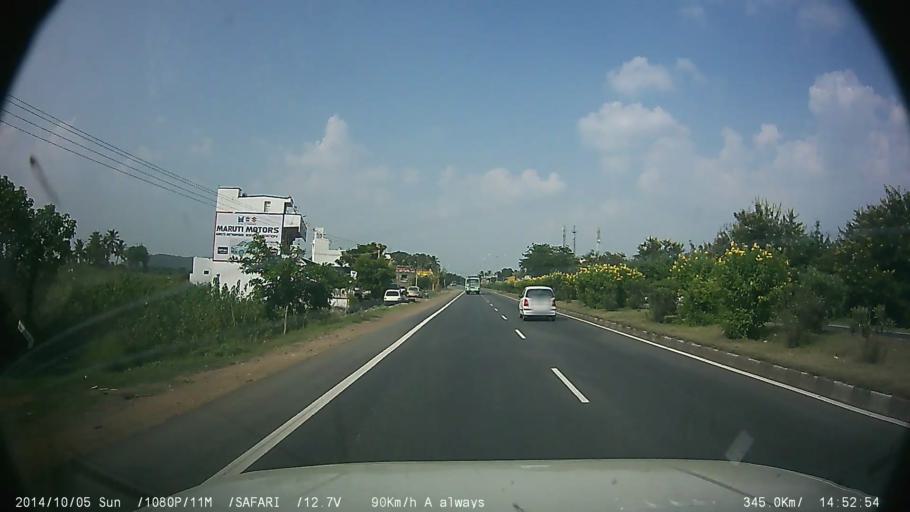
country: IN
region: Tamil Nadu
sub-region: Kancheepuram
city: Madurantakam
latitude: 12.5301
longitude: 79.8994
